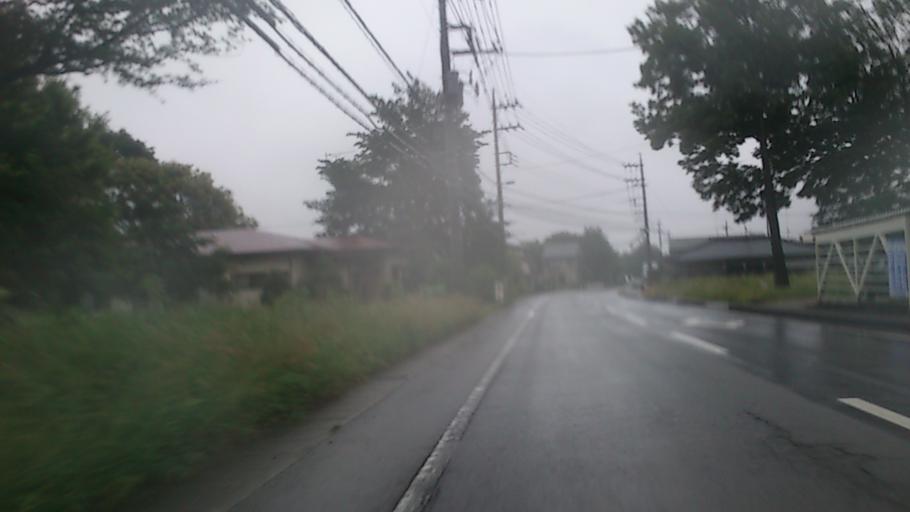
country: JP
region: Tochigi
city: Otawara
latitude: 36.9124
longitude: 139.9801
